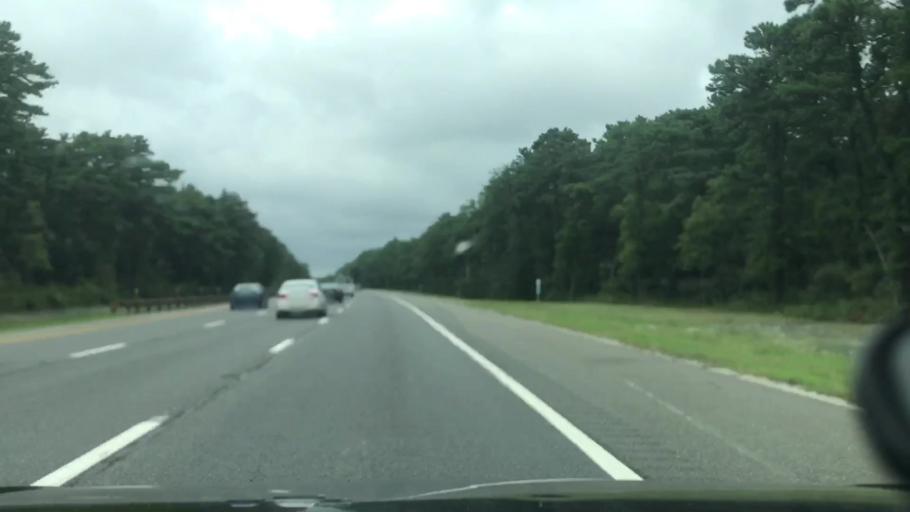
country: US
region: New Jersey
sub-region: Ocean County
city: Forked River
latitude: 39.8323
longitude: -74.2248
